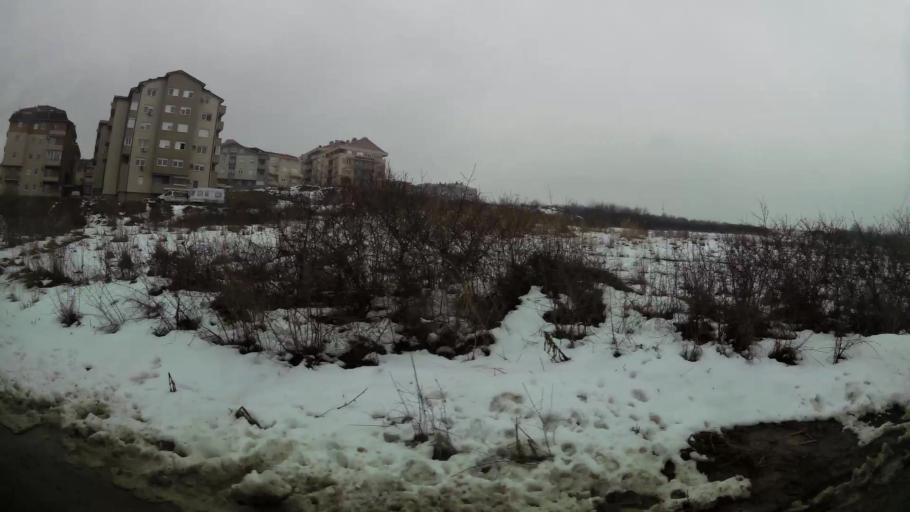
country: RS
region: Central Serbia
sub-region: Belgrade
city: Zvezdara
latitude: 44.7587
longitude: 20.5065
